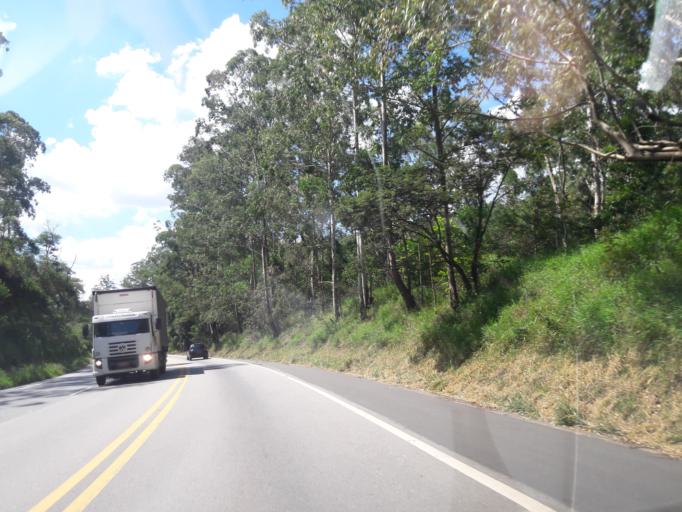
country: BR
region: Sao Paulo
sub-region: Francisco Morato
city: Francisco Morato
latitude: -23.2617
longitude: -46.7913
